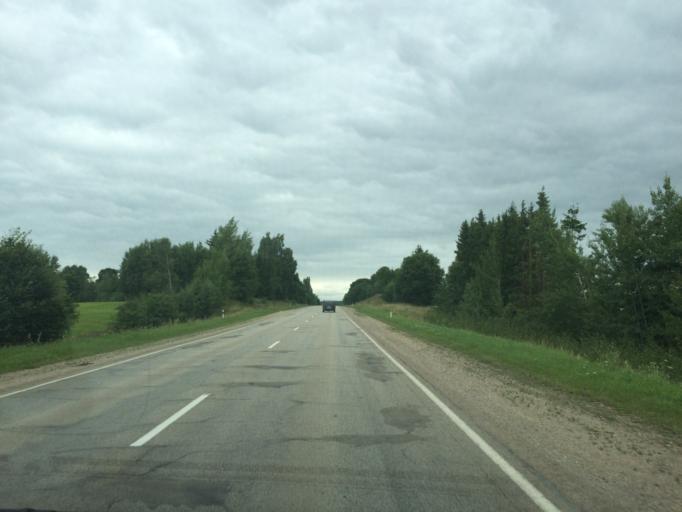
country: LV
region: Rezekne
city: Rezekne
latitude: 56.5559
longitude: 27.3610
